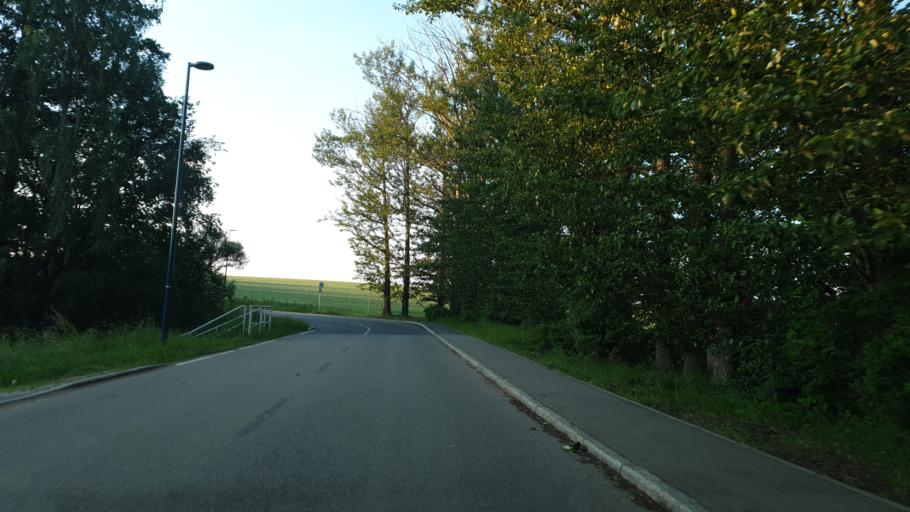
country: DE
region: Saxony
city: Oelsnitz
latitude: 50.6997
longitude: 12.7228
